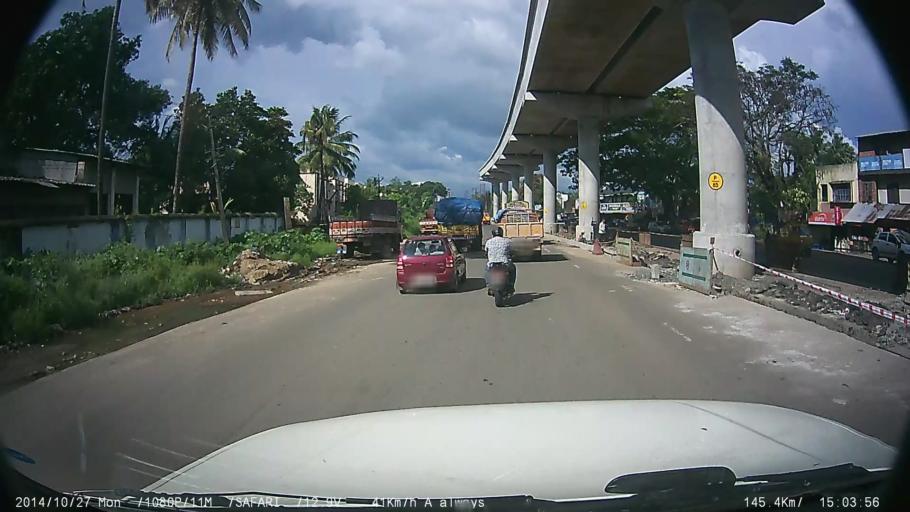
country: IN
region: Kerala
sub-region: Ernakulam
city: Aluva
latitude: 10.0928
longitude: 76.3459
